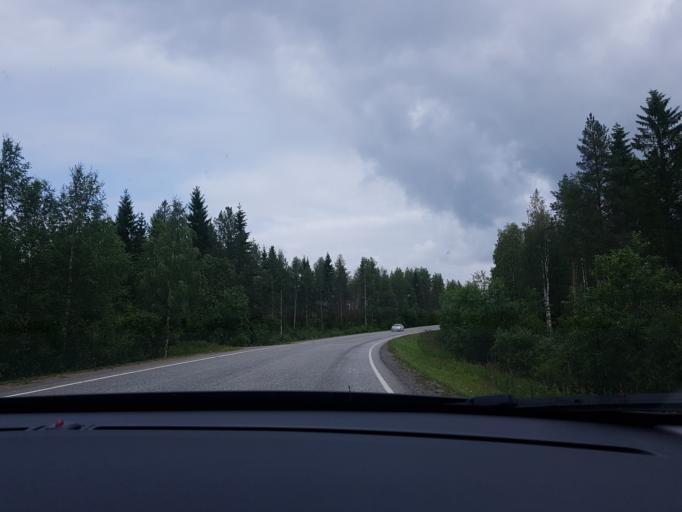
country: FI
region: Kainuu
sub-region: Kehys-Kainuu
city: Kuhmo
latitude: 64.1412
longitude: 29.4558
